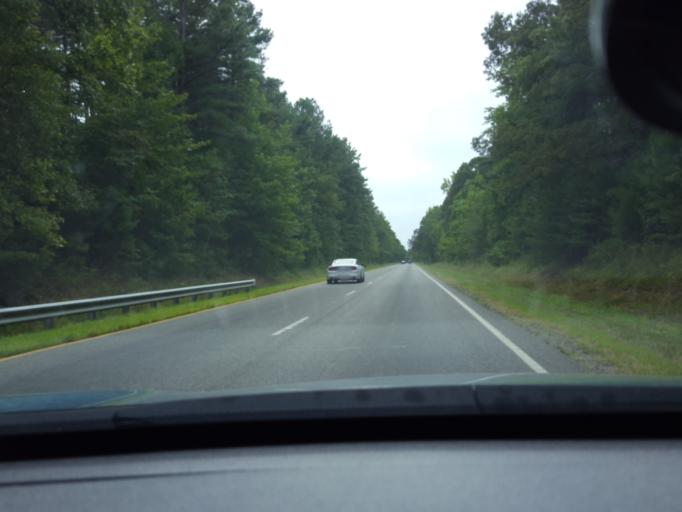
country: US
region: Virginia
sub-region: Caroline County
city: Bowling Green
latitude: 38.1219
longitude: -77.2498
